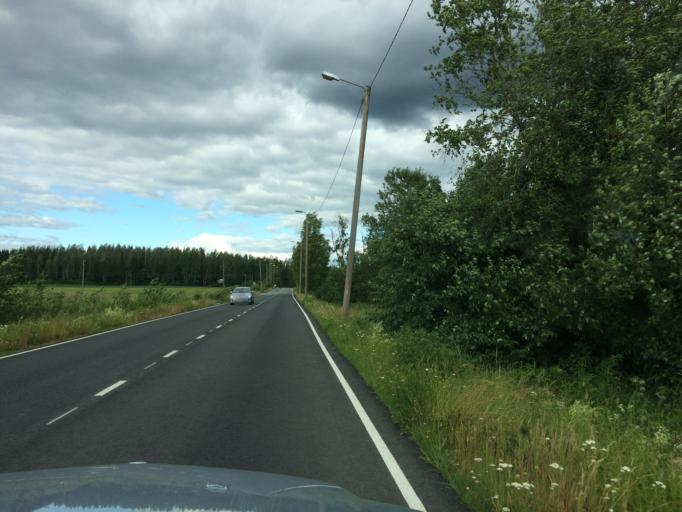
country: FI
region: Haeme
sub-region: Haemeenlinna
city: Haemeenlinna
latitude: 61.0211
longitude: 24.4131
